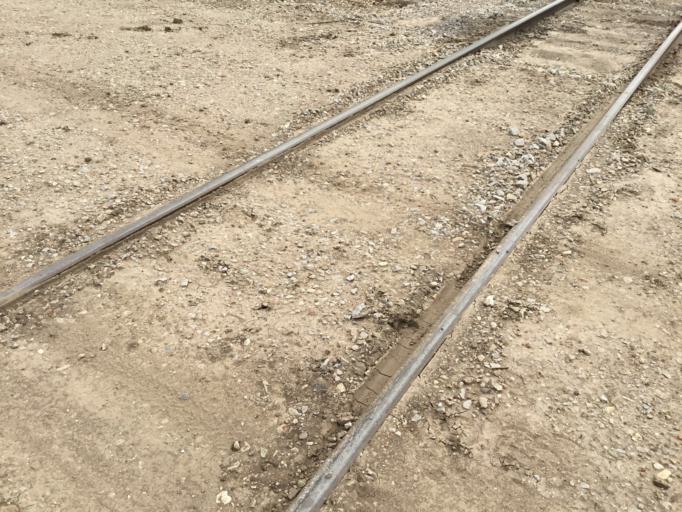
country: US
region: Kansas
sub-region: Jewell County
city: Mankato
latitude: 39.7791
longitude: -97.9330
